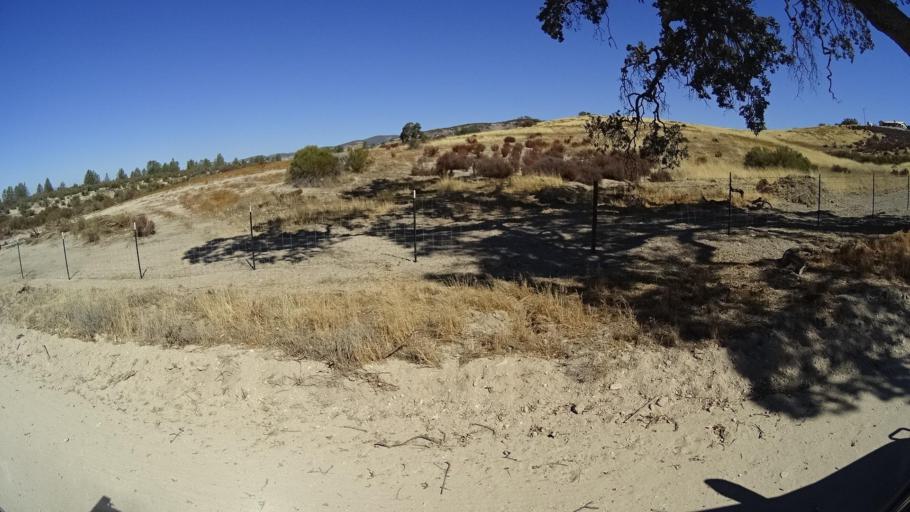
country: US
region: California
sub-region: Monterey County
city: King City
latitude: 35.9509
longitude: -121.0720
